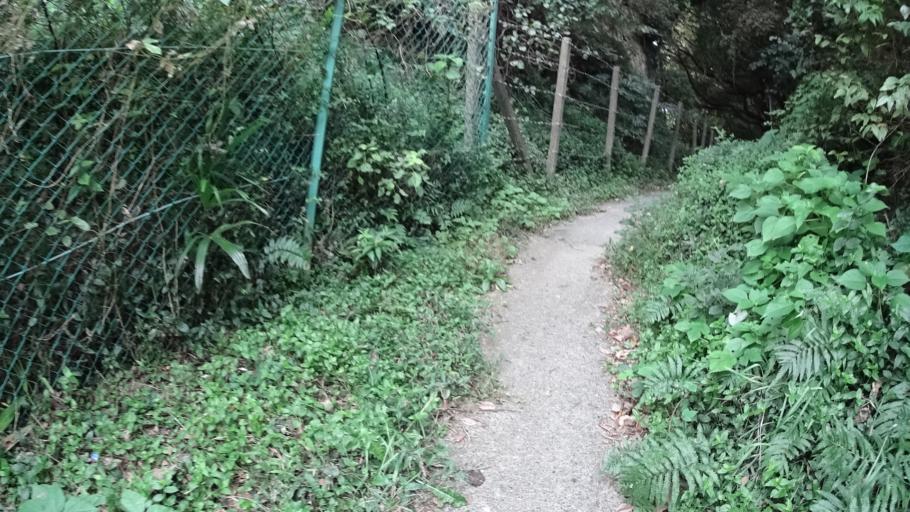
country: JP
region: Kanagawa
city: Zushi
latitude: 35.2980
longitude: 139.6198
